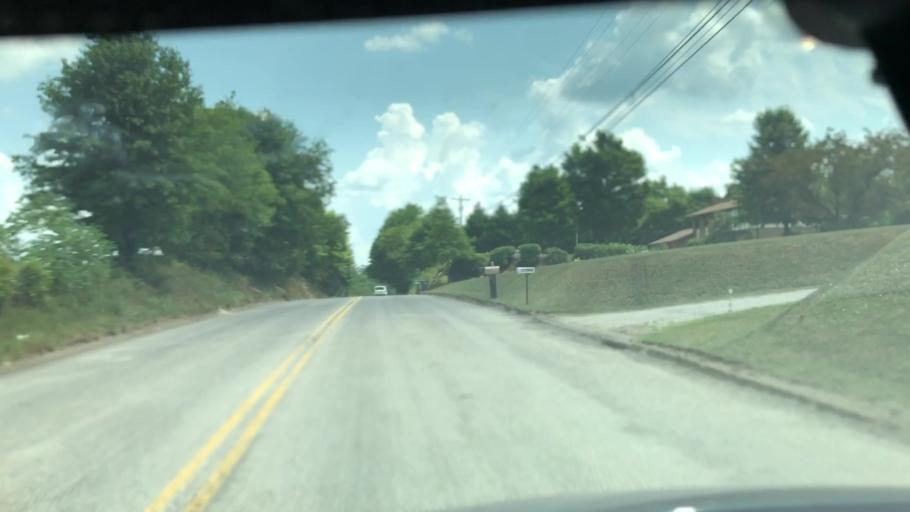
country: US
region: Pennsylvania
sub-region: Butler County
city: Saxonburg
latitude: 40.7892
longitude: -79.8058
